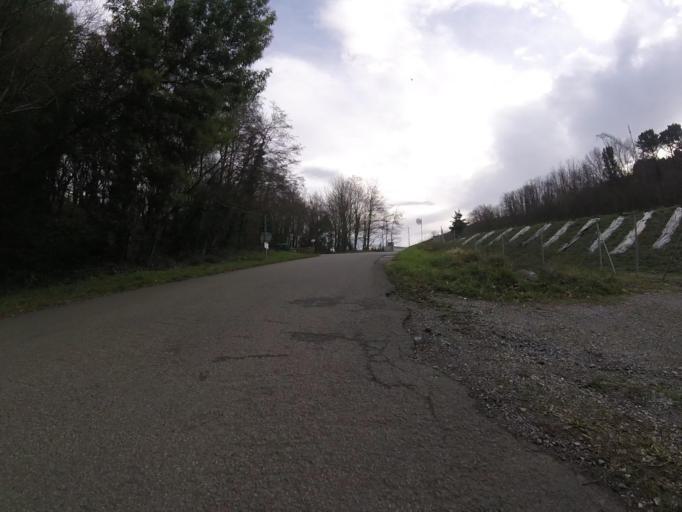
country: FR
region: Aquitaine
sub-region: Departement des Pyrenees-Atlantiques
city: Urrugne
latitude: 43.3420
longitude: -1.7294
